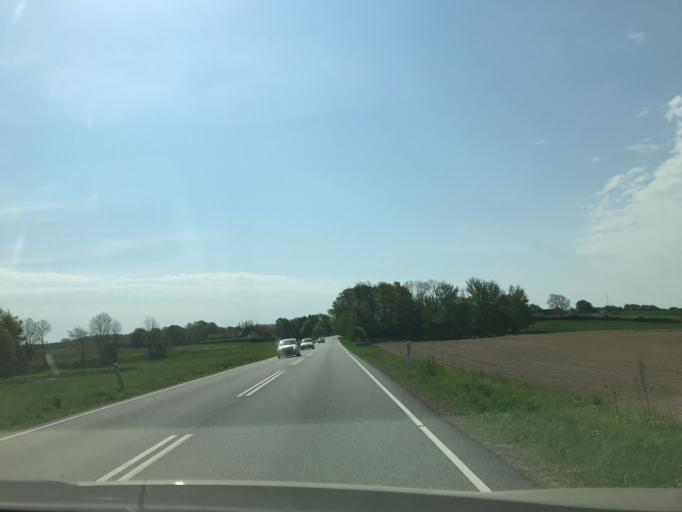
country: DK
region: South Denmark
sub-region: Middelfart Kommune
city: Ejby
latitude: 55.3522
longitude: 9.9359
